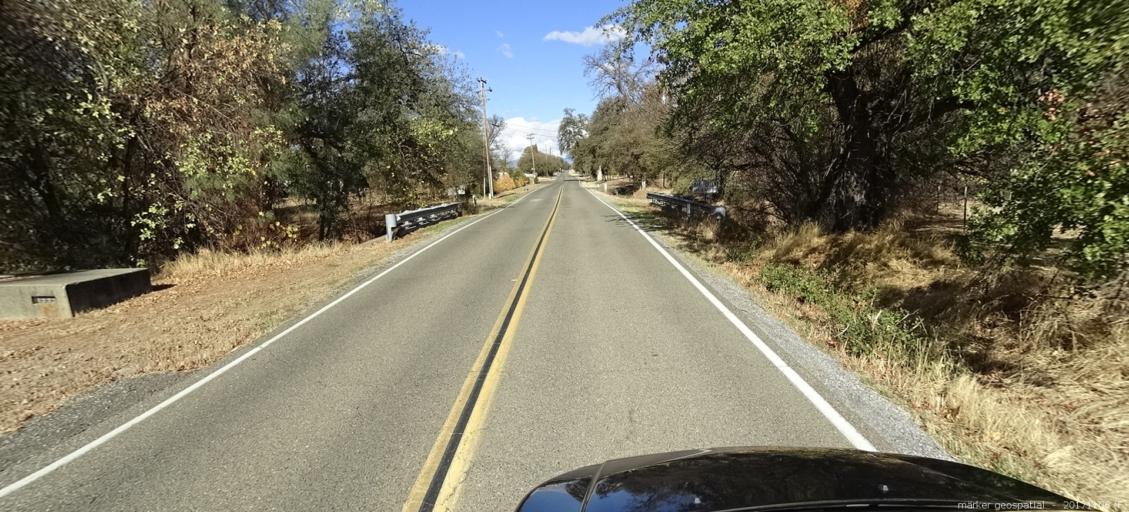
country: US
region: California
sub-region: Shasta County
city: Palo Cedro
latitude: 40.5735
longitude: -122.2199
